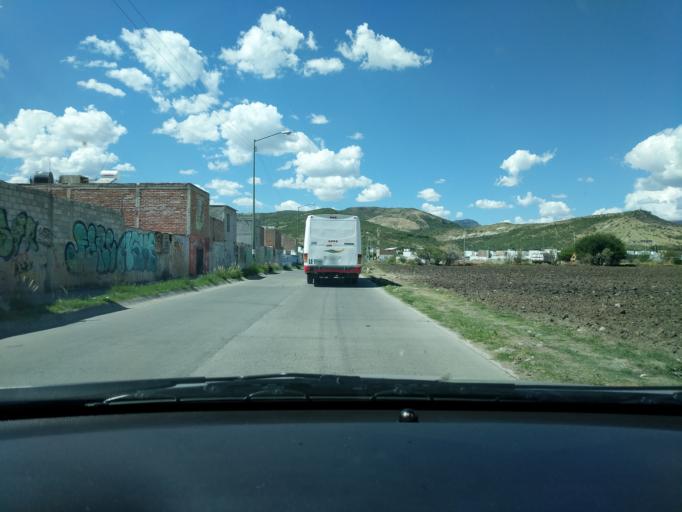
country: MX
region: Guanajuato
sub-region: Leon
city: Fraccionamiento Paraiso Real
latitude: 21.1018
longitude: -101.5781
